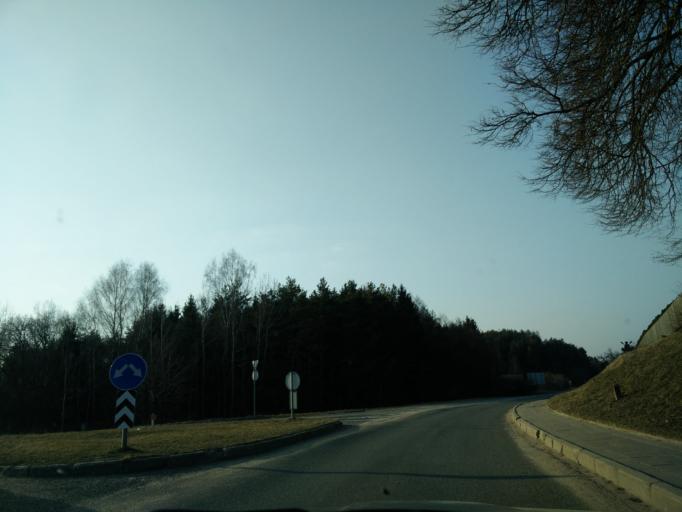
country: LT
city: Trakai
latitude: 54.6535
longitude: 24.9180
